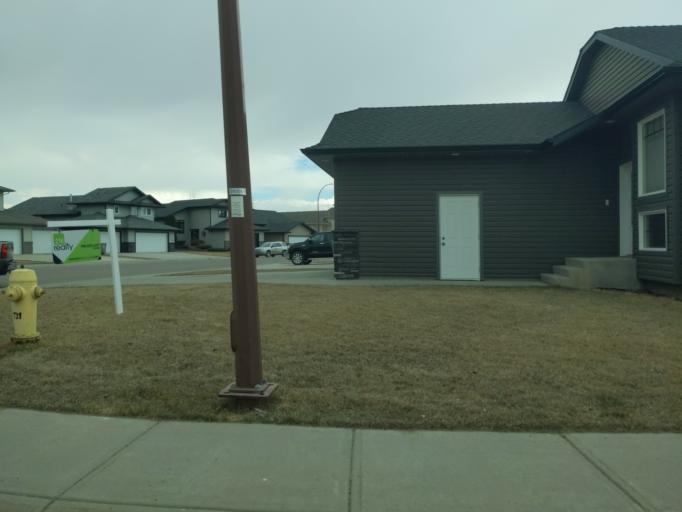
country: CA
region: Saskatchewan
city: Lloydminster
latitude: 53.2737
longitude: -110.0511
